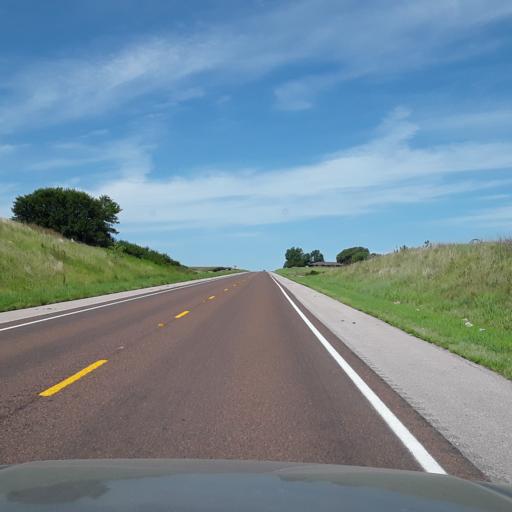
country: US
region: Nebraska
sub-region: Lancaster County
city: Lincoln
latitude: 40.8866
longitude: -96.8421
